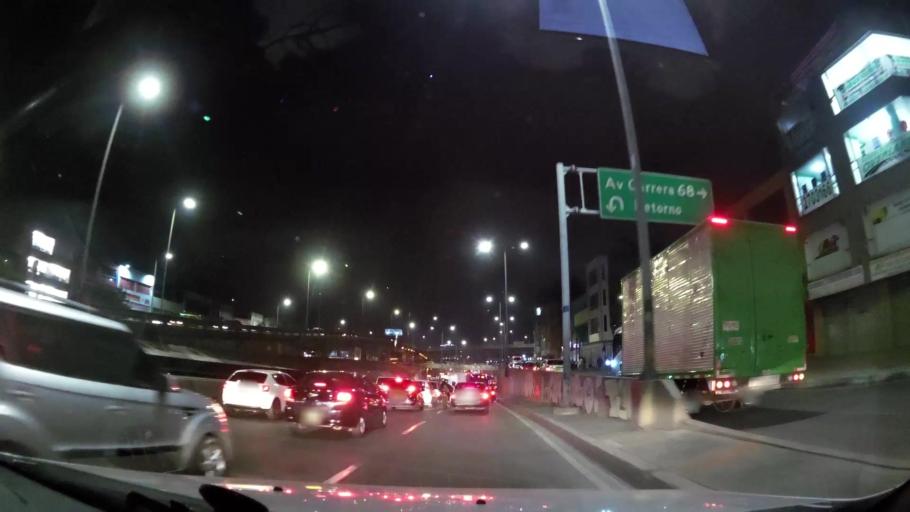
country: CO
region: Bogota D.C.
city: Bogota
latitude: 4.5949
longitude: -74.1365
